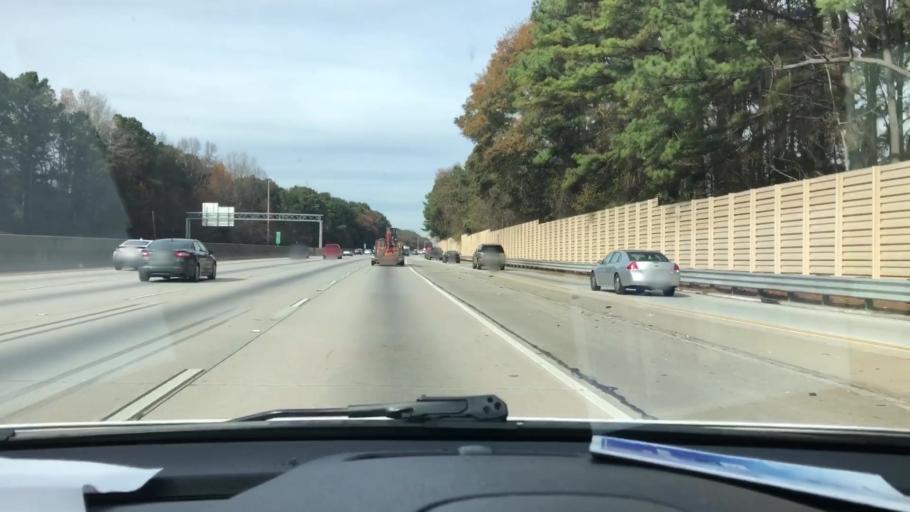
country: US
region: Georgia
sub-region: DeKalb County
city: Belvedere Park
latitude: 33.7545
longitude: -84.2320
